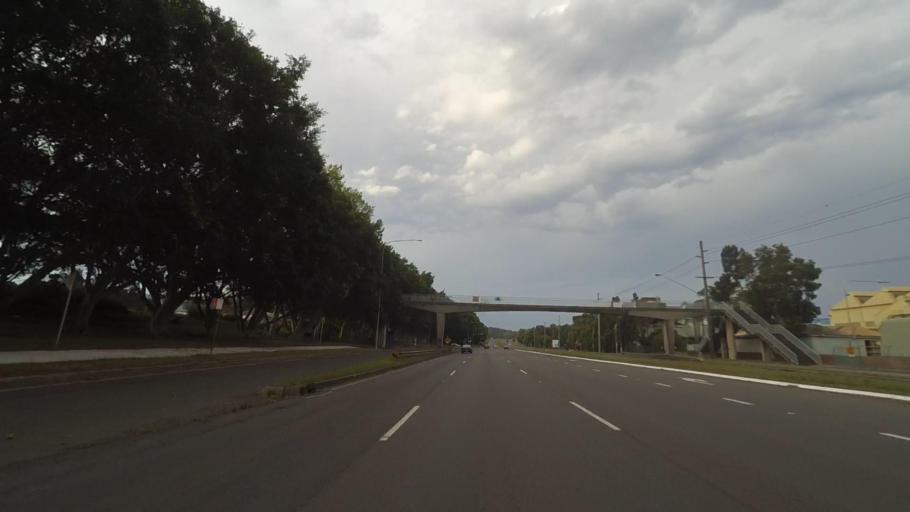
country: AU
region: New South Wales
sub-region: Wollongong
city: Coniston
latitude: -34.4565
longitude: 150.8732
